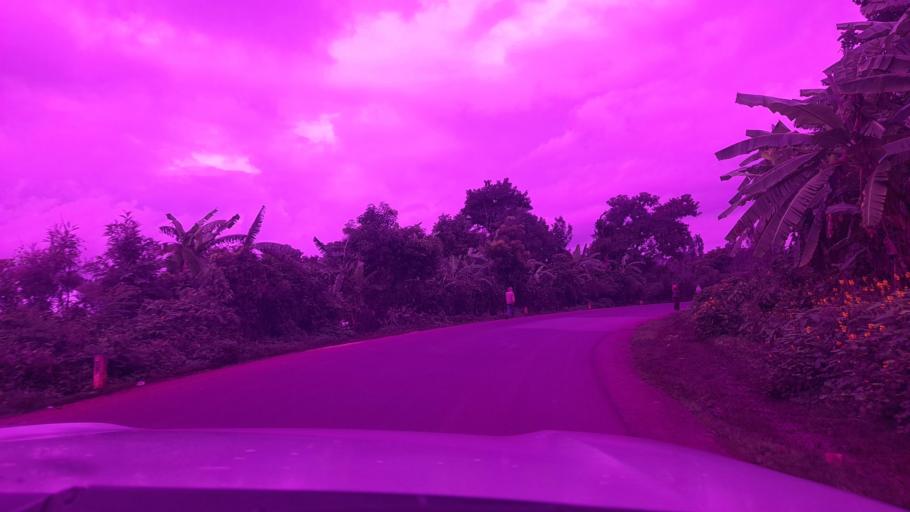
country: ET
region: Oromiya
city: Jima
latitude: 7.9232
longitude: 37.4097
